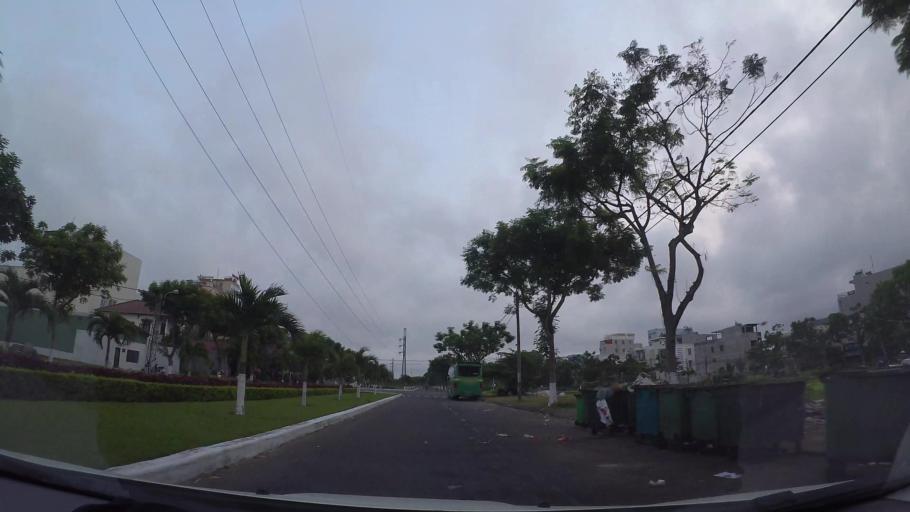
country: VN
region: Da Nang
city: Son Tra
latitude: 16.0474
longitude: 108.2361
